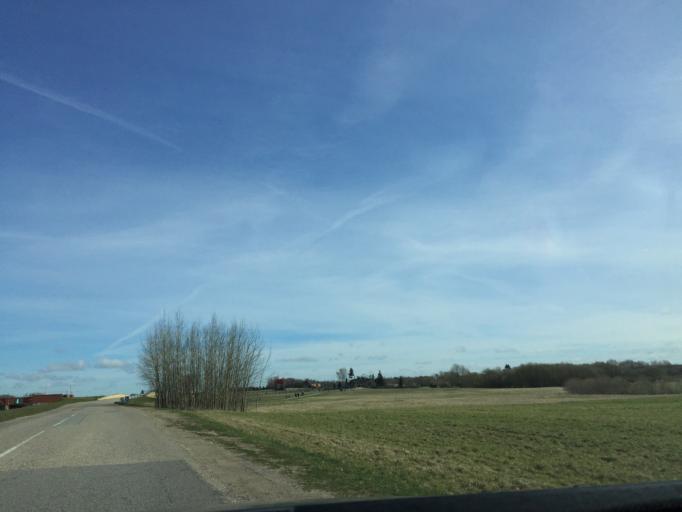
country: LT
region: Siauliu apskritis
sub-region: Siauliai
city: Siauliai
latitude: 56.0132
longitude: 23.4077
